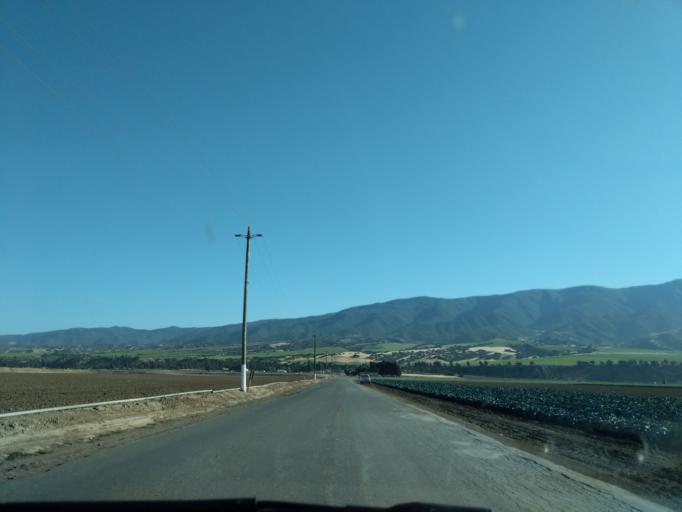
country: US
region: California
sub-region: Monterey County
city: Soledad
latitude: 36.4059
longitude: -121.3592
